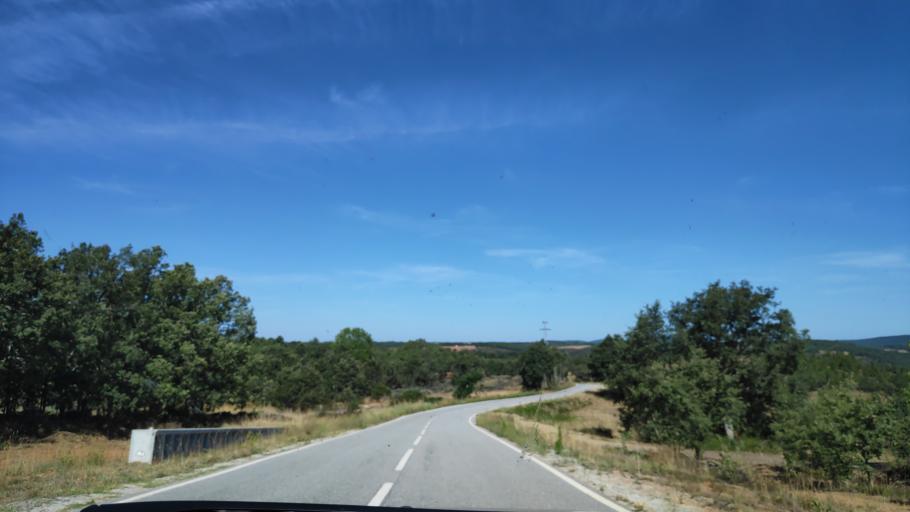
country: ES
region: Castille and Leon
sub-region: Provincia de Zamora
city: Alcanices
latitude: 41.6247
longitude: -6.3464
